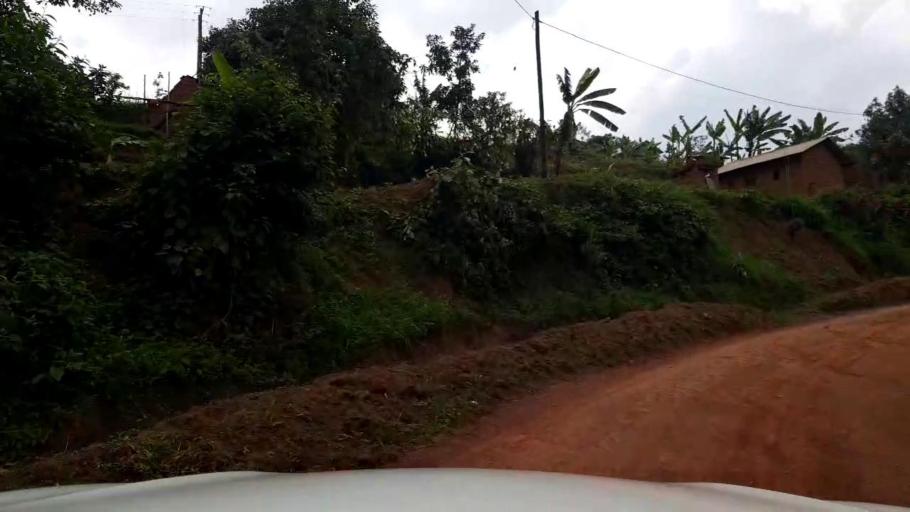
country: RW
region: Northern Province
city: Byumba
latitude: -1.4869
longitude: 29.9094
